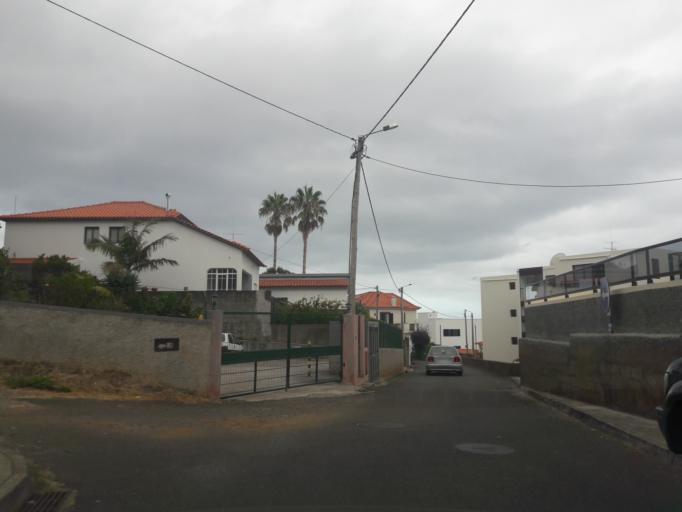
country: PT
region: Madeira
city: Canico
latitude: 32.6441
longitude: -16.8511
